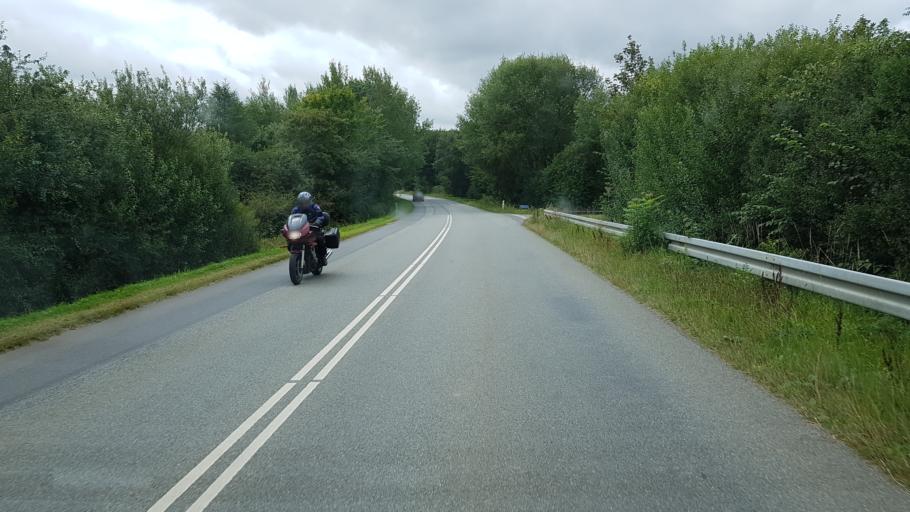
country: DK
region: South Denmark
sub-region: Kolding Kommune
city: Kolding
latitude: 55.4673
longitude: 9.3871
